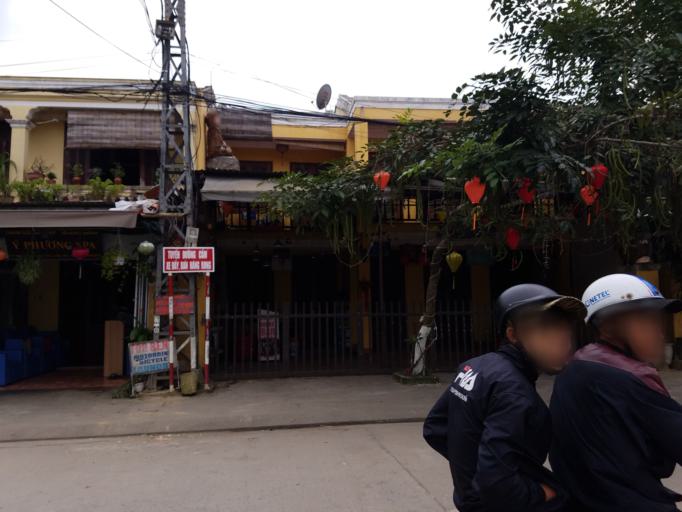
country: VN
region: Quang Nam
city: Hoi An
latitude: 15.8763
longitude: 108.3245
